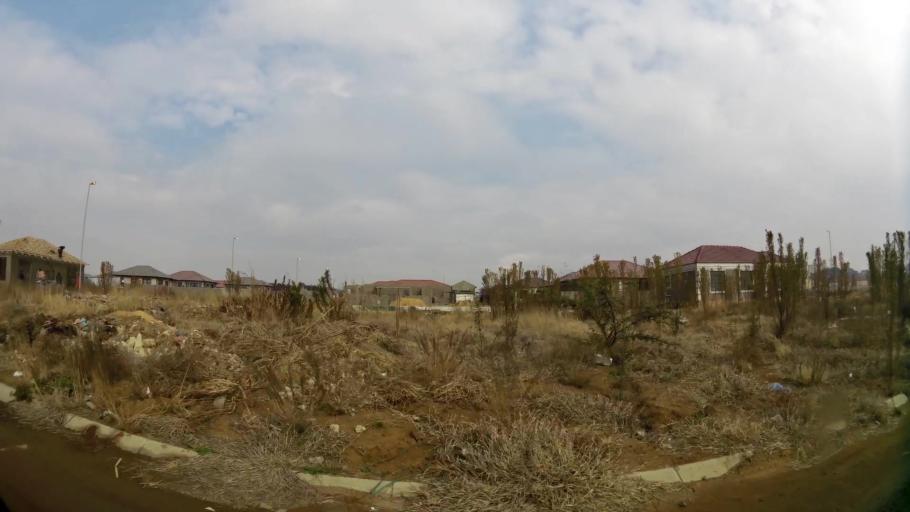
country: ZA
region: Gauteng
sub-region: Sedibeng District Municipality
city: Vanderbijlpark
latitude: -26.6798
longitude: 27.8439
